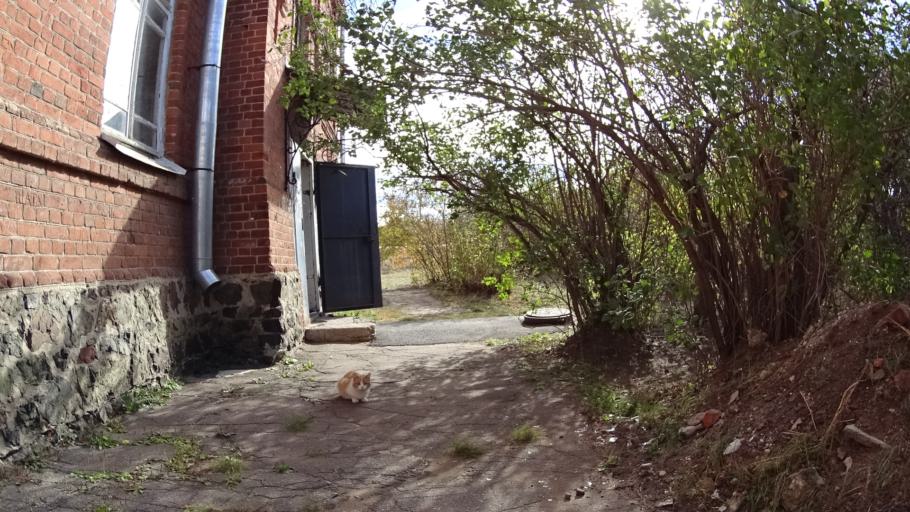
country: RU
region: Chelyabinsk
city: Troitsk
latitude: 54.0783
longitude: 61.5846
